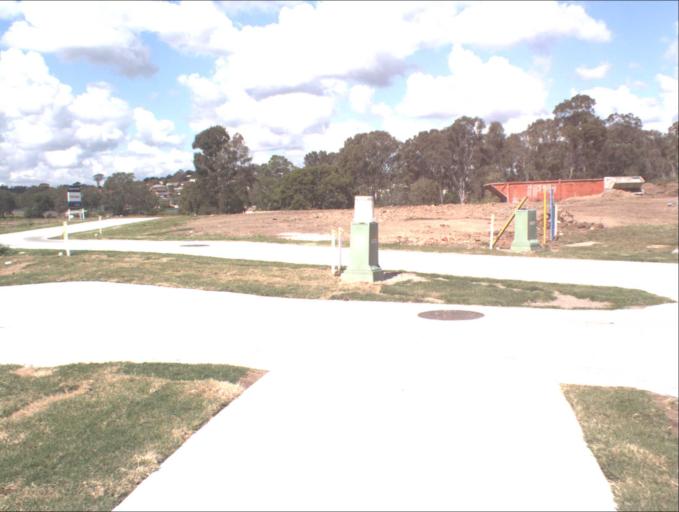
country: AU
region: Queensland
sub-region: Logan
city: Waterford West
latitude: -27.6910
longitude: 153.1648
